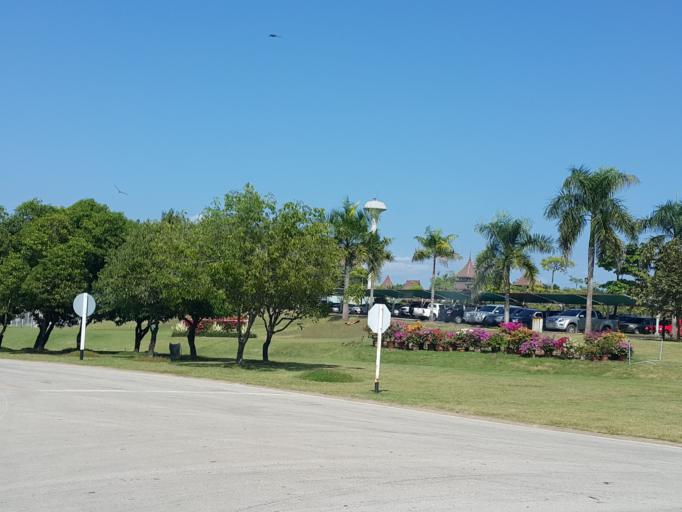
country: TH
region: Lampang
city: Mae Mo
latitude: 18.3188
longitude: 99.7436
